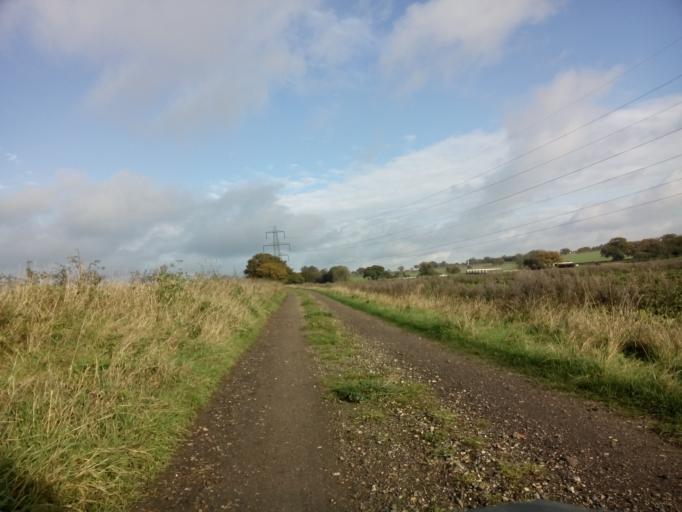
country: GB
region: England
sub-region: Suffolk
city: Needham Market
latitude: 52.1527
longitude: 1.0758
